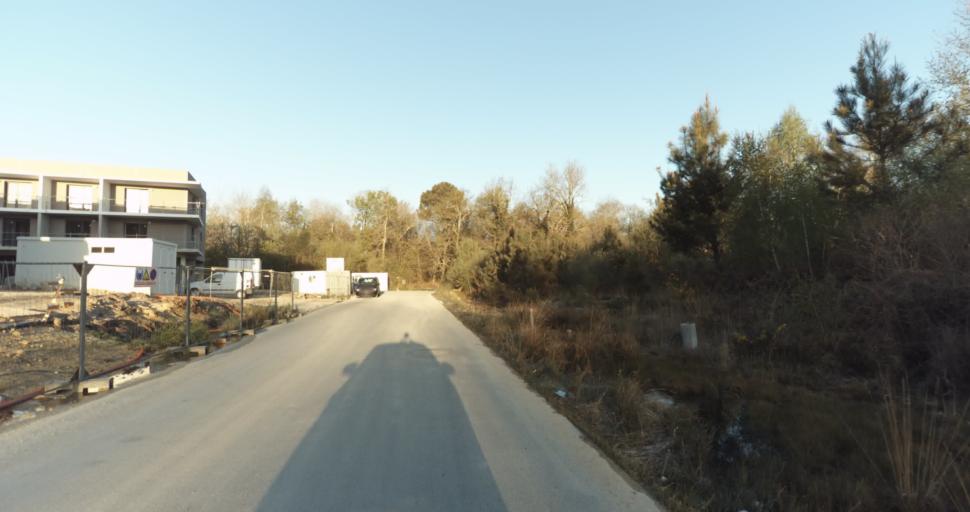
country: FR
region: Aquitaine
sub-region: Departement de la Gironde
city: Martignas-sur-Jalle
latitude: 44.8108
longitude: -0.7700
